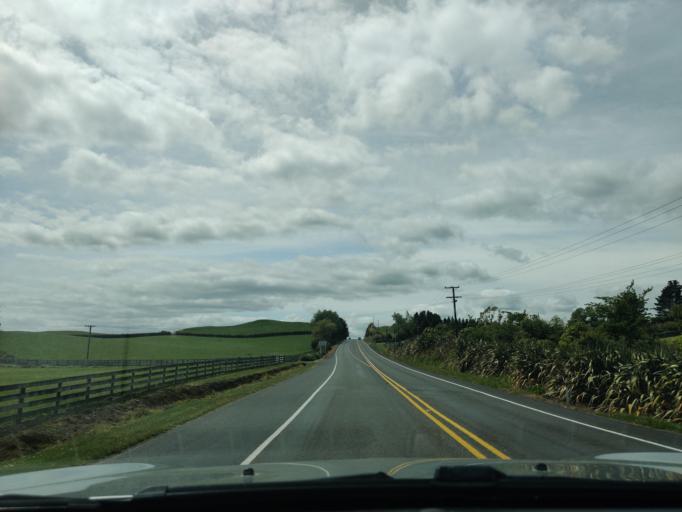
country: NZ
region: Taranaki
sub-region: New Plymouth District
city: New Plymouth
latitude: -39.1512
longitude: 174.1609
